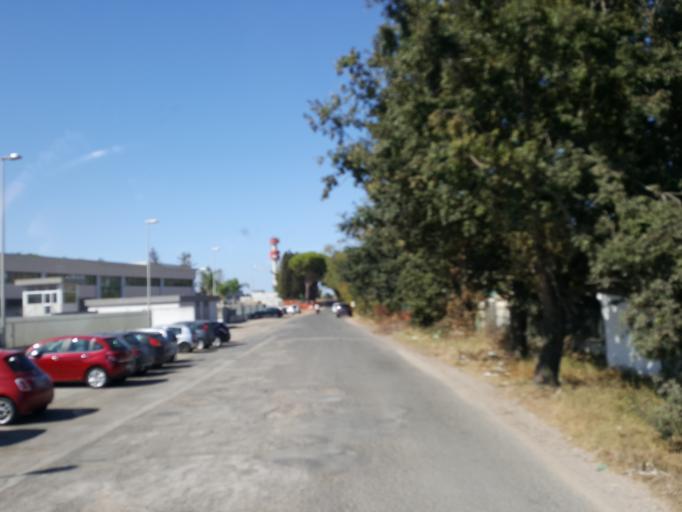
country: IT
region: Latium
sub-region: Citta metropolitana di Roma Capitale
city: Anzio
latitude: 41.5149
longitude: 12.6255
